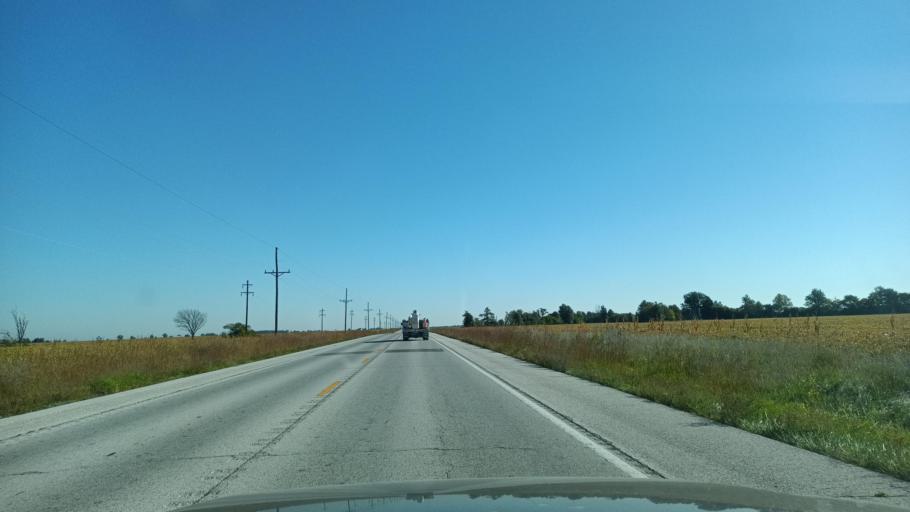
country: US
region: Missouri
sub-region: Audrain County
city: Vandalia
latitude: 39.4672
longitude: -91.6001
